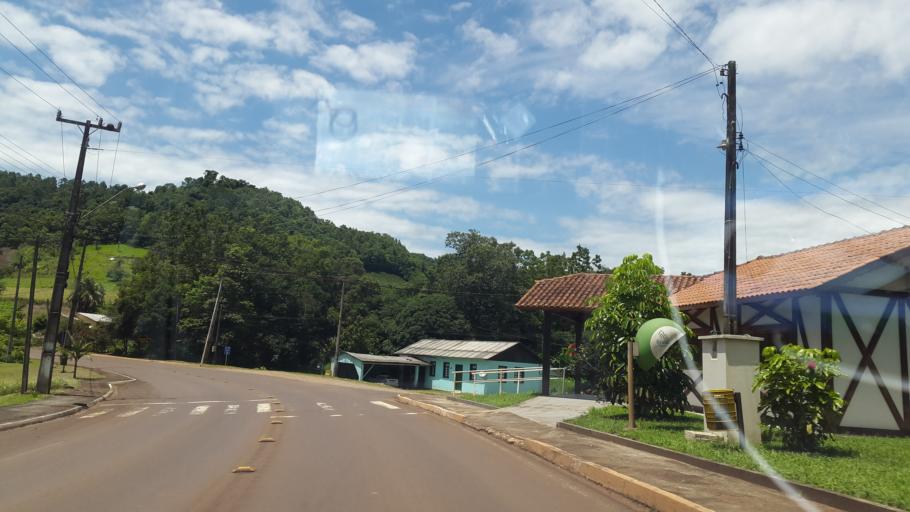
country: BR
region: Rio Grande do Sul
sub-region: Frederico Westphalen
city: Frederico Westphalen
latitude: -27.0721
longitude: -53.4289
